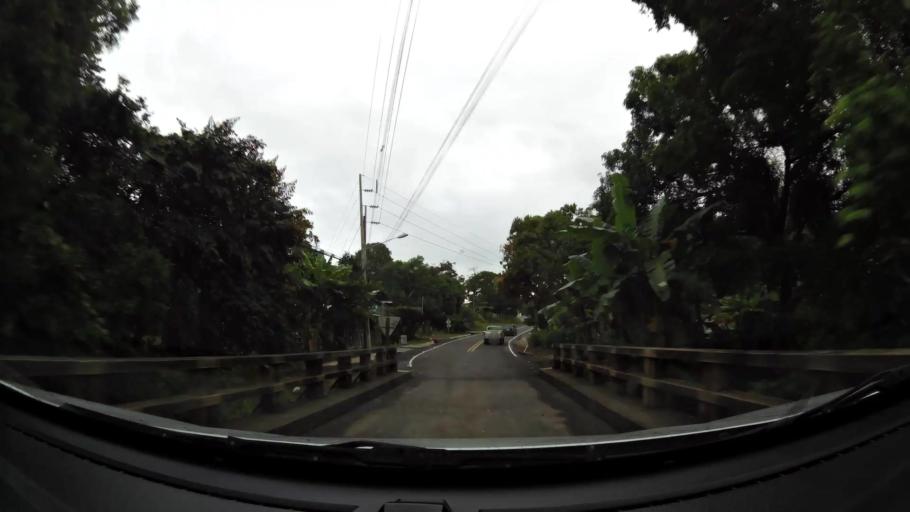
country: CR
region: Alajuela
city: Desamparados
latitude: 9.9412
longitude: -84.5386
